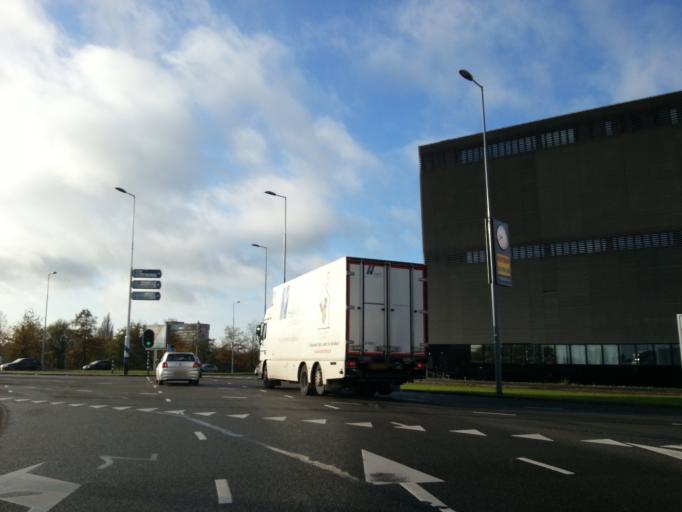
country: NL
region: South Holland
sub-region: Gemeente Rotterdam
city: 's-Gravenland
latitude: 51.8947
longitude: 4.5283
